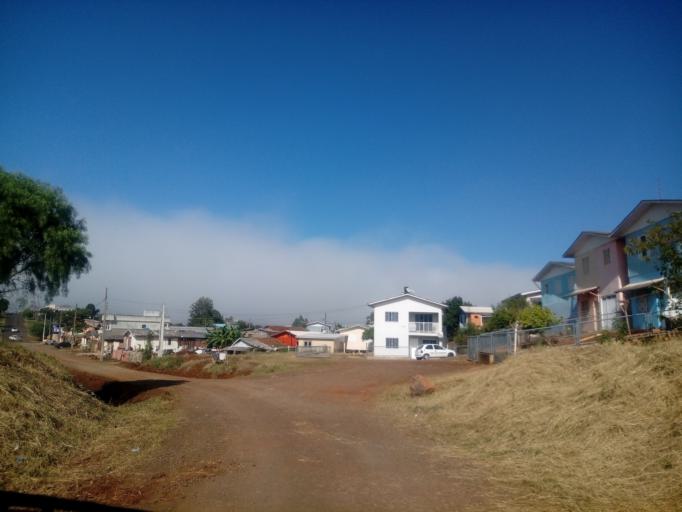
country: BR
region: Santa Catarina
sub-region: Chapeco
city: Chapeco
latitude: -27.0785
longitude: -52.6107
